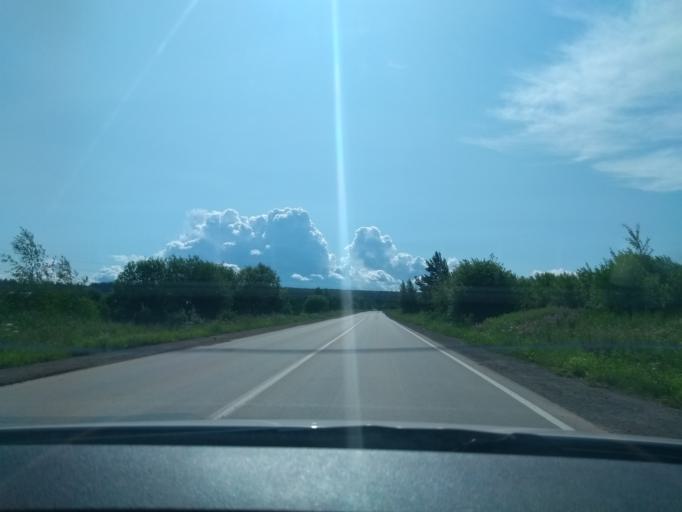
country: RU
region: Perm
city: Lobanovo
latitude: 57.8447
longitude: 56.3605
